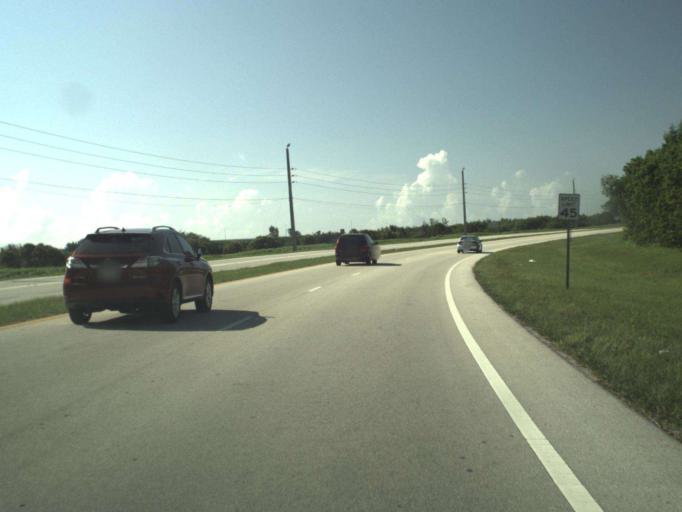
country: US
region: Florida
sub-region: Indian River County
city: Vero Beach
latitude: 27.6598
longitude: -80.3854
